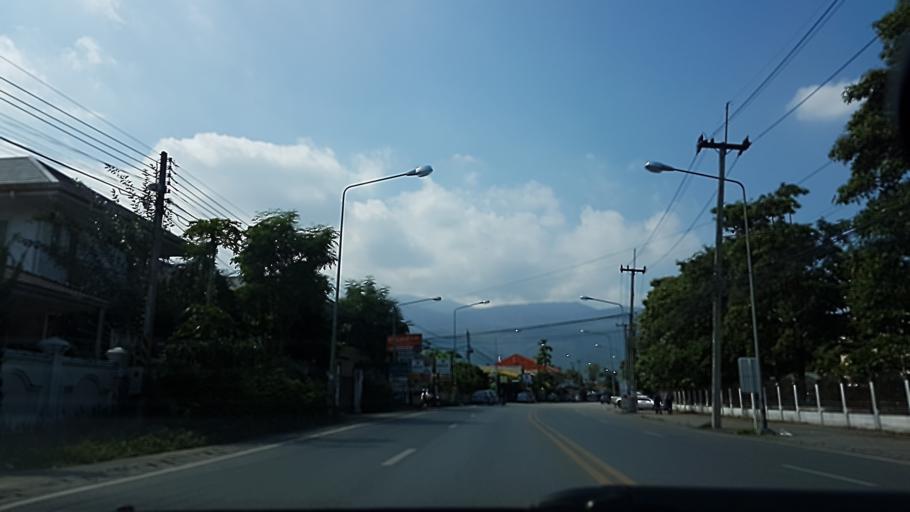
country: TH
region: Chiang Mai
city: Chiang Mai
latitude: 18.8188
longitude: 98.9748
